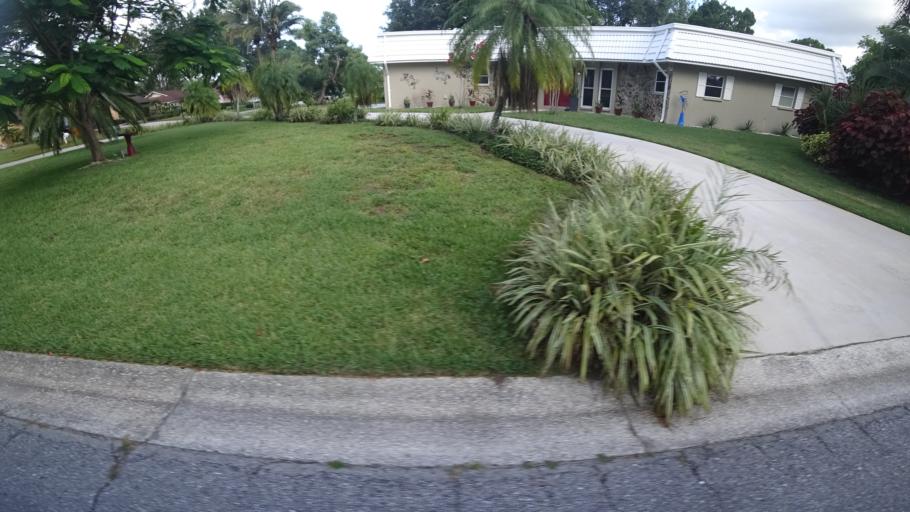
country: US
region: Florida
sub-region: Sarasota County
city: Desoto Lakes
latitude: 27.4022
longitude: -82.4955
